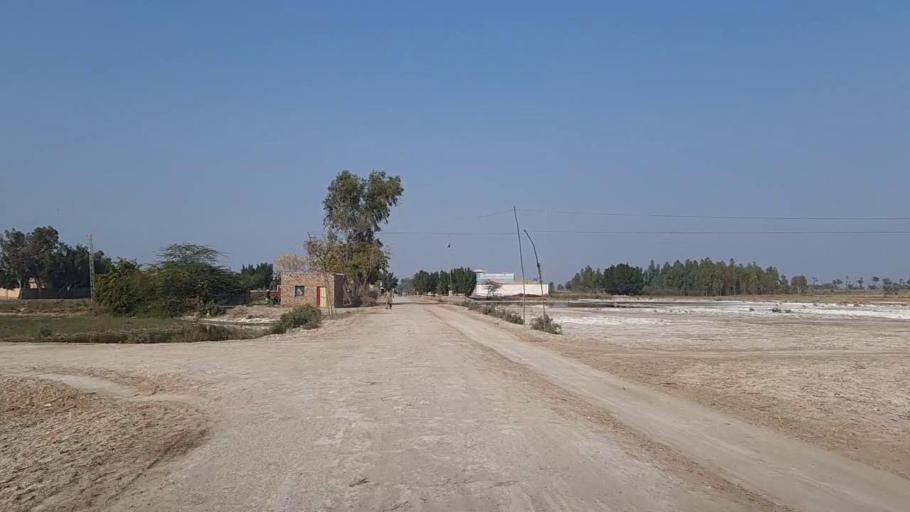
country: PK
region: Sindh
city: Daur
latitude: 26.4250
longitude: 68.4089
